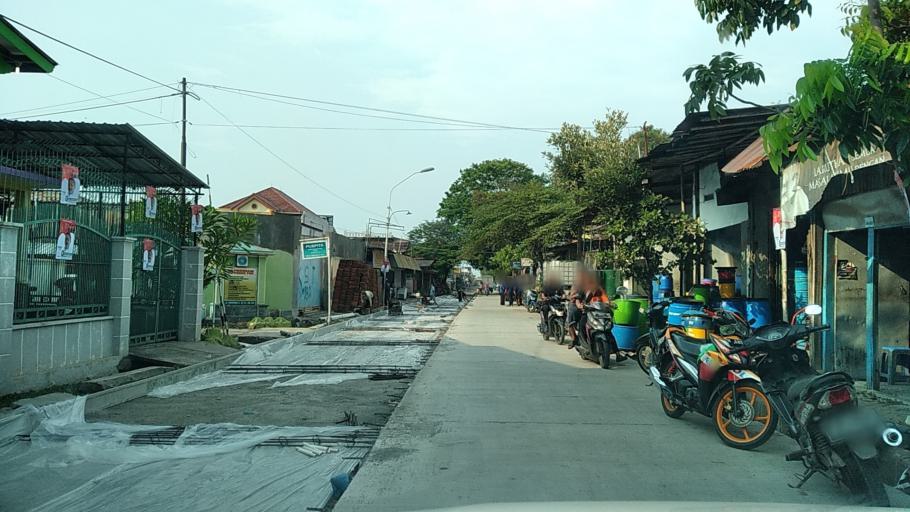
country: ID
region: Central Java
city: Semarang
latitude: -6.9777
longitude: 110.4413
